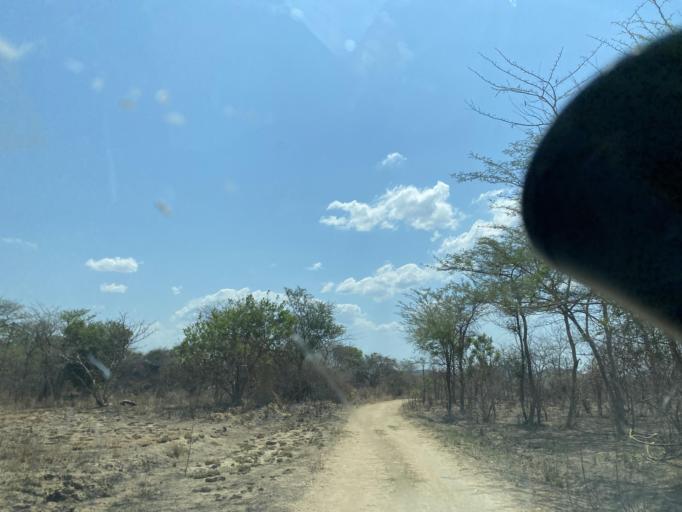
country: ZM
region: Lusaka
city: Chongwe
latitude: -15.0821
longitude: 29.5054
